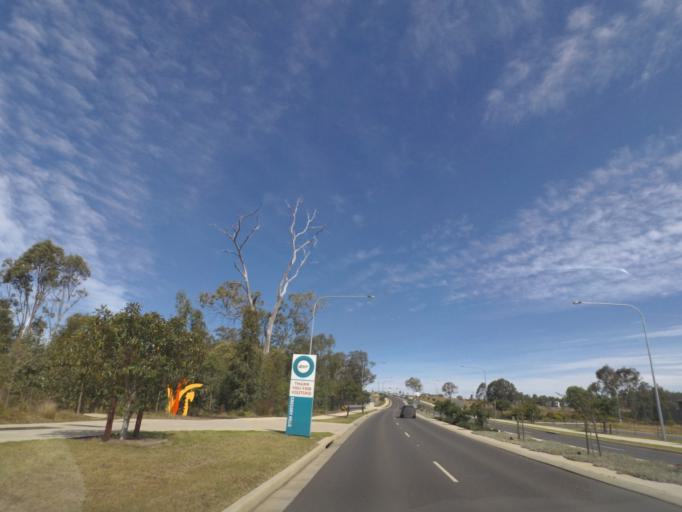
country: AU
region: New South Wales
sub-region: Camden
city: Narellan Vale
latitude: -34.0289
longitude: 150.7867
